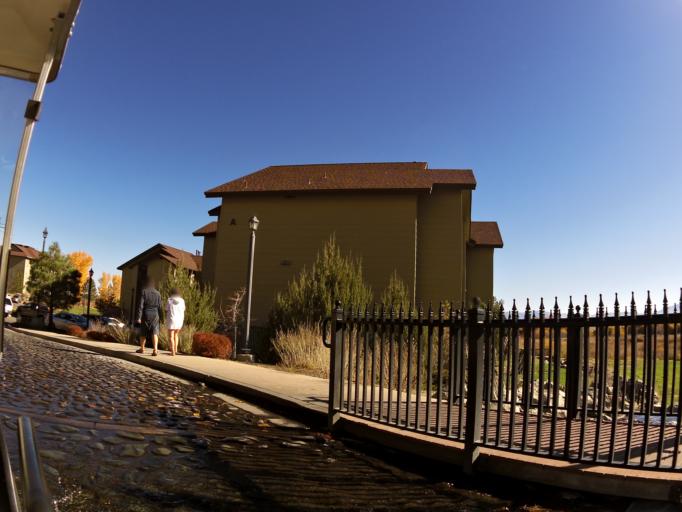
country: US
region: Nevada
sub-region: Douglas County
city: Minden
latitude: 38.9818
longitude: -119.8330
